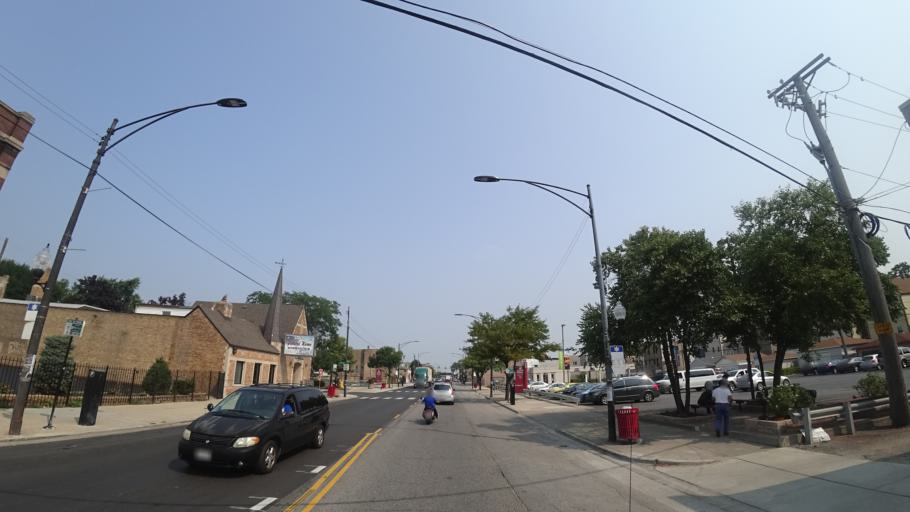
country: US
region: Illinois
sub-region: Cook County
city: Cicero
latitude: 41.8447
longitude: -87.7246
